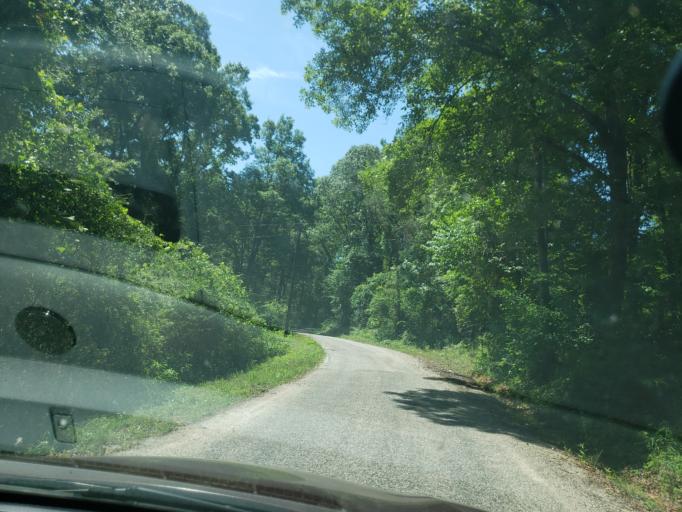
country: US
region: Alabama
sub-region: Elmore County
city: Tallassee
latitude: 32.5925
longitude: -85.8765
